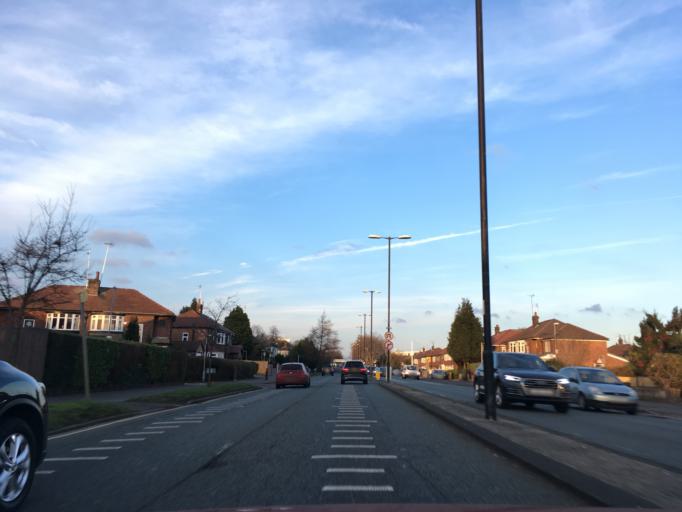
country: GB
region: England
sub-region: Manchester
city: Didsbury
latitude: 53.4044
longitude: -2.2233
